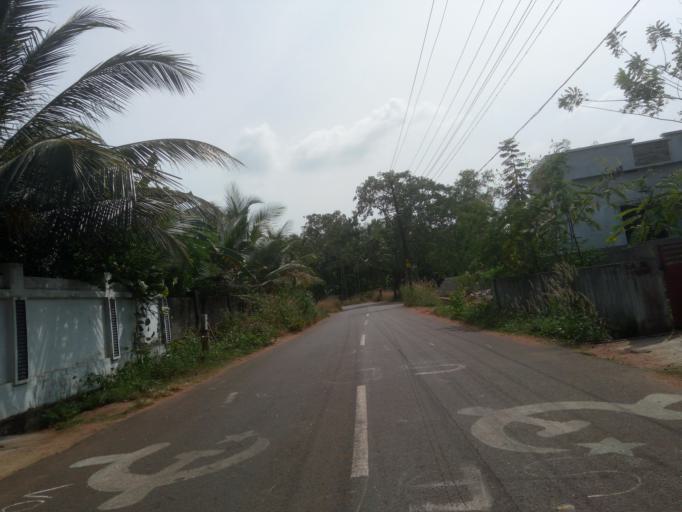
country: IN
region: Kerala
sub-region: Malappuram
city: Ponnani
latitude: 10.8046
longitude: 76.0338
